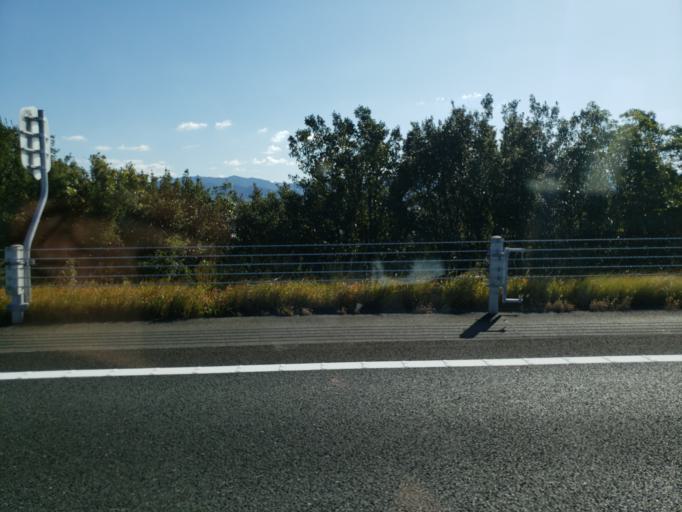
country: JP
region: Hyogo
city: Fukura
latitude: 34.3054
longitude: 134.7434
